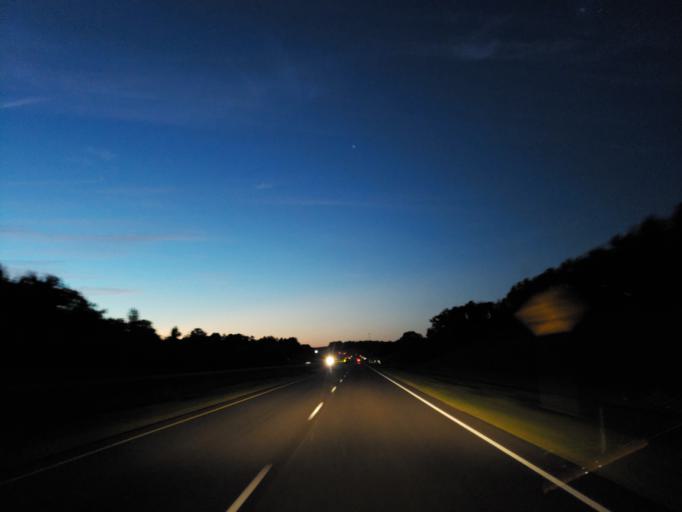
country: US
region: Mississippi
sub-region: Clarke County
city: Quitman
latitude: 32.0949
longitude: -88.7021
